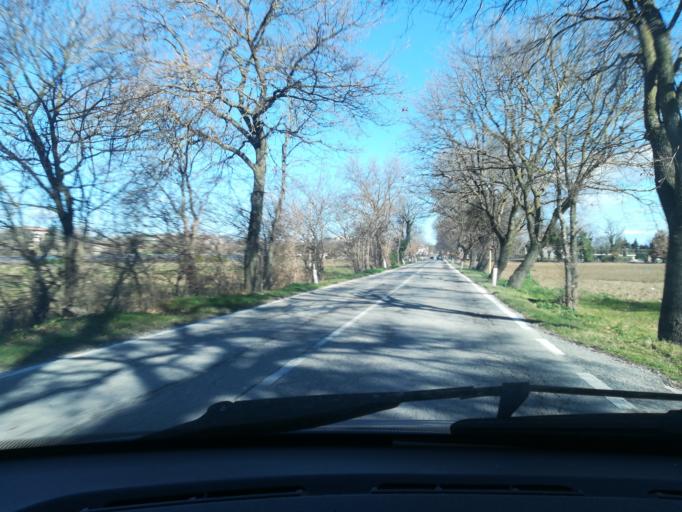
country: IT
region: The Marches
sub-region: Provincia di Macerata
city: Villa Potenza
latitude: 43.3351
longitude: 13.4275
